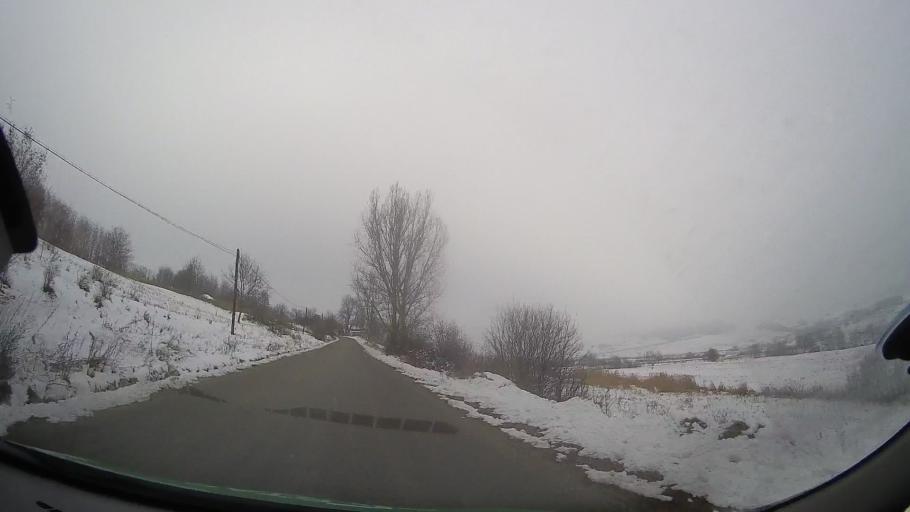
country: RO
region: Bacau
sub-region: Comuna Huruesti
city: Huruesti
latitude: 46.3076
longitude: 27.2931
